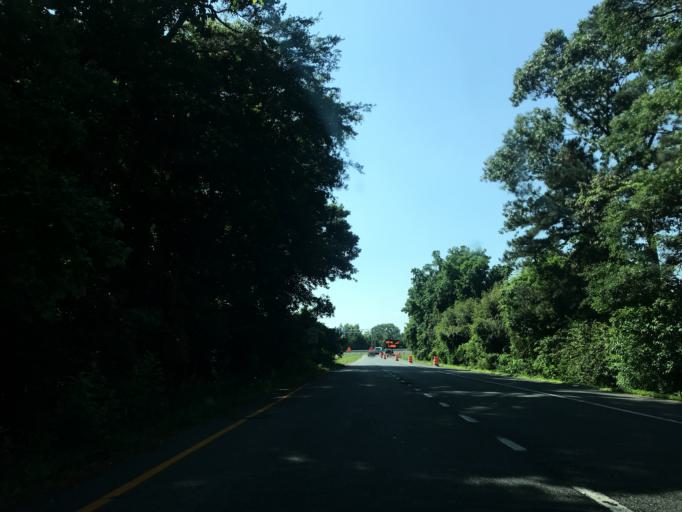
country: US
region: Maryland
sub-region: Wicomico County
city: Salisbury
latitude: 38.3716
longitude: -75.5362
